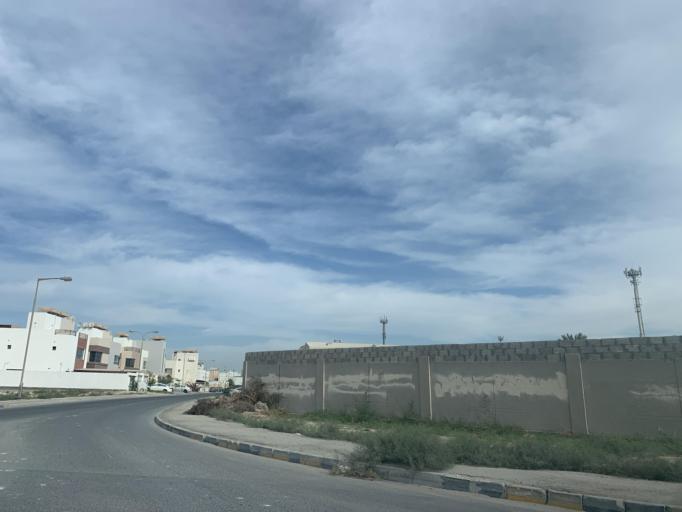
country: BH
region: Central Governorate
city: Madinat Hamad
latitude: 26.1182
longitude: 50.4749
